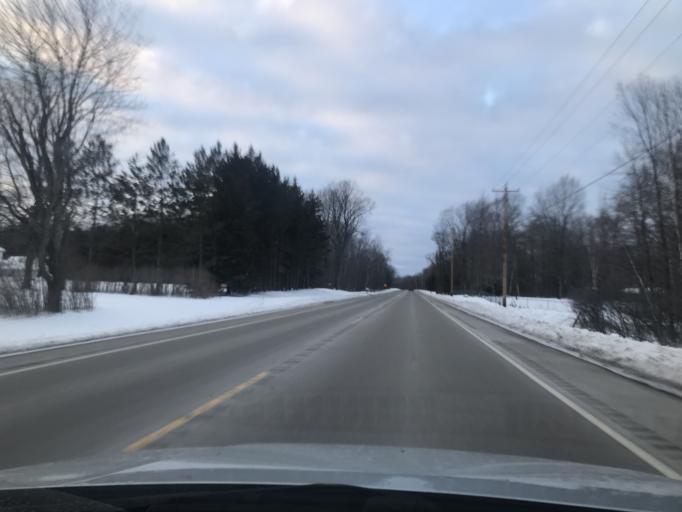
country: US
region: Wisconsin
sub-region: Marinette County
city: Marinette
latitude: 45.1492
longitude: -87.7026
